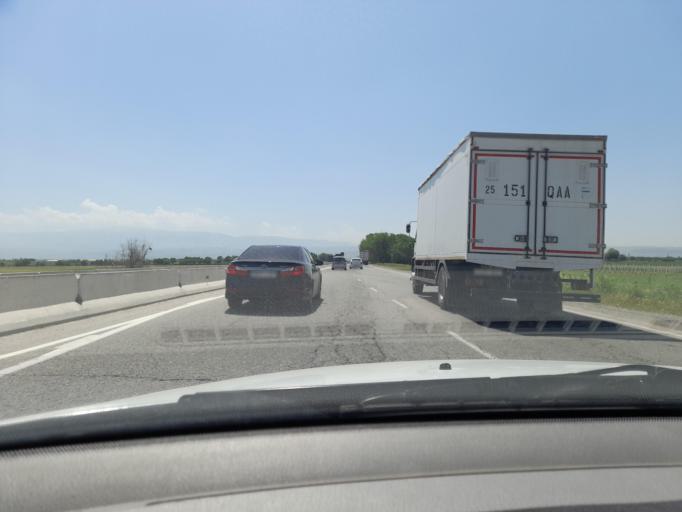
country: UZ
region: Jizzax
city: Jizzax
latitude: 40.1188
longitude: 67.9474
